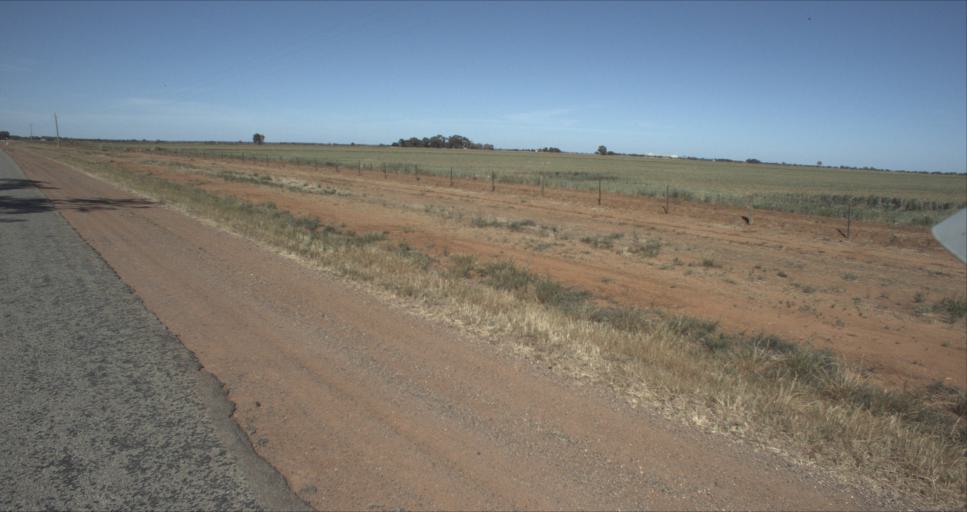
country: AU
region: New South Wales
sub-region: Leeton
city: Leeton
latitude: -34.5465
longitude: 146.3155
